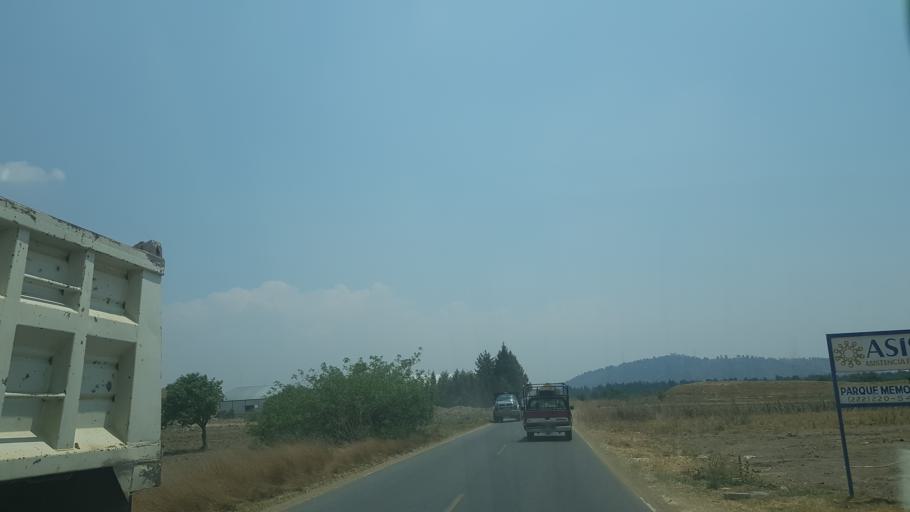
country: MX
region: Puebla
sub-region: San Jeronimo Tecuanipan
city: San Miguel Papaxtla
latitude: 19.0906
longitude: -98.3846
